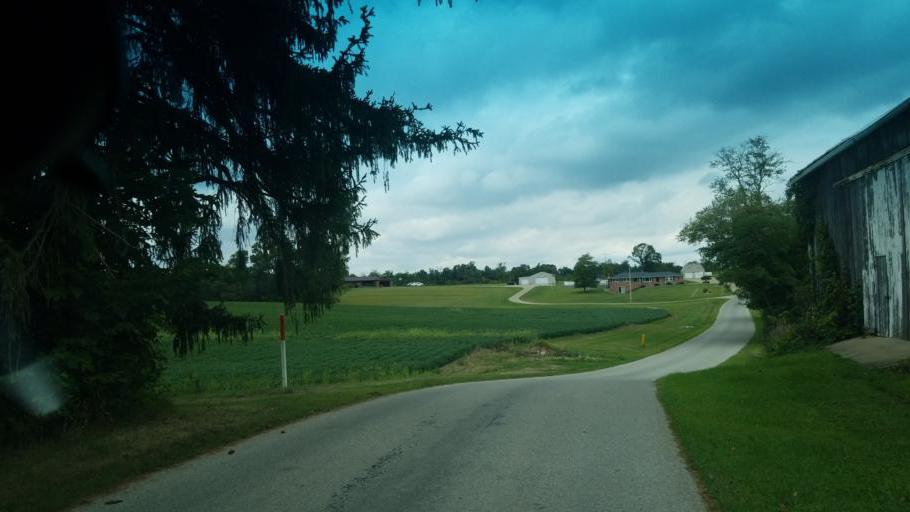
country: US
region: Ohio
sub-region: Richland County
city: Ontario
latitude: 40.8148
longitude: -82.5625
